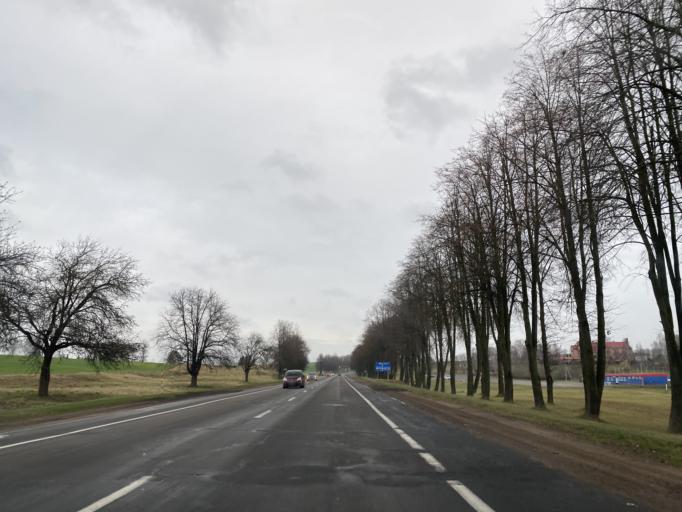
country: BY
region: Minsk
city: Horad Smalyavichy
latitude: 54.0448
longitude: 28.0622
